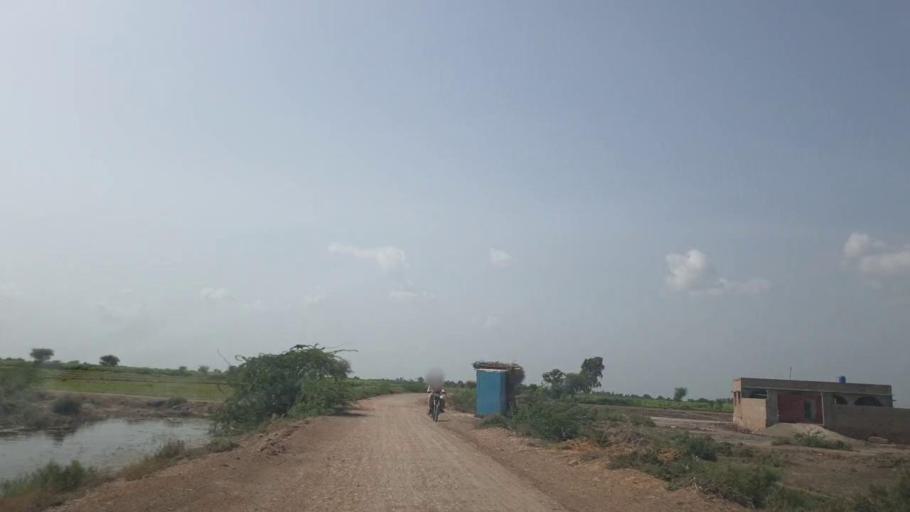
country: PK
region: Sindh
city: Tando Bago
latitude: 24.7699
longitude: 69.1308
